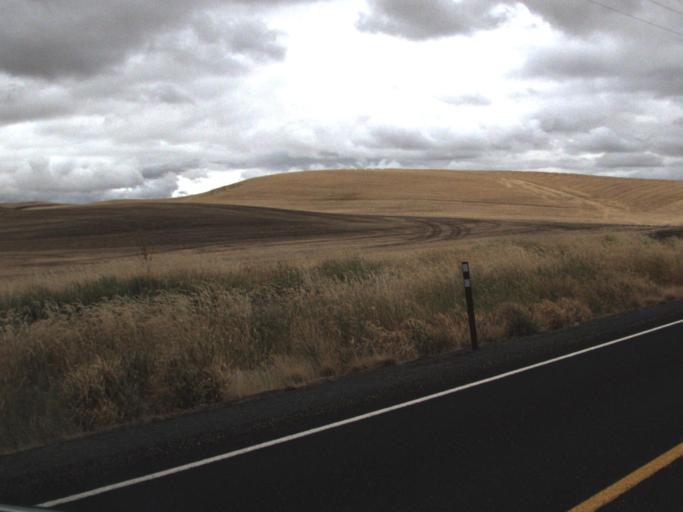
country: US
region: Washington
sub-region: Whitman County
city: Colfax
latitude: 47.1864
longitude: -117.3119
